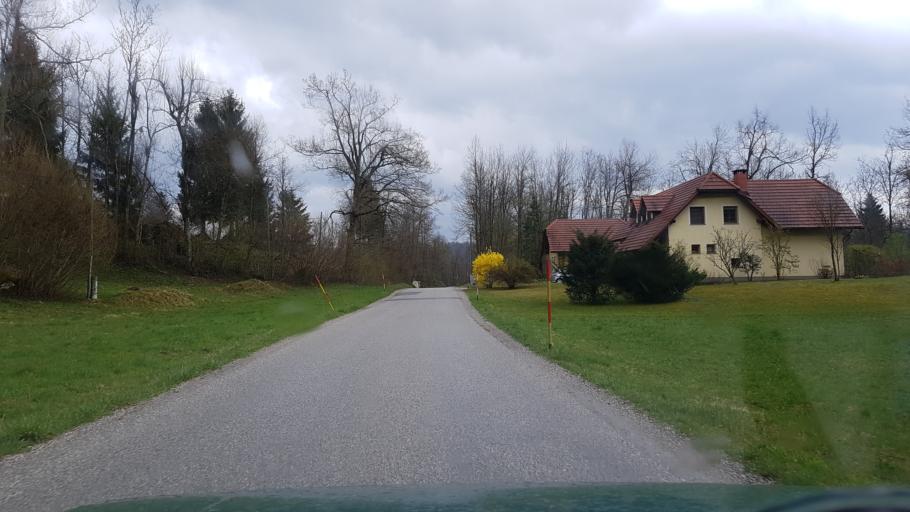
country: SI
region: Cerkno
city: Cerkno
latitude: 46.1173
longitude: 13.8624
